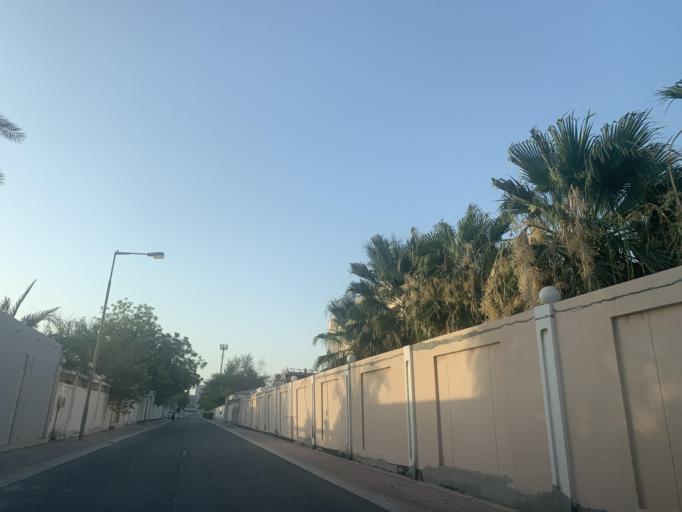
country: BH
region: Manama
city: Jidd Hafs
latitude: 26.1998
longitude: 50.5253
